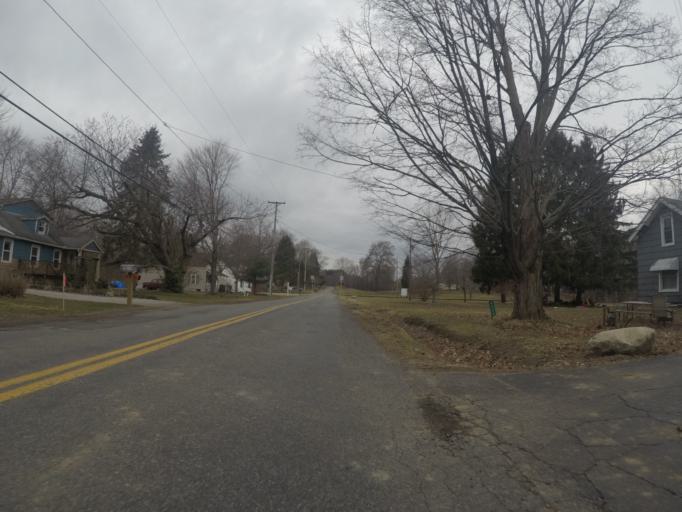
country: US
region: Ohio
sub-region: Portage County
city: Ravenna
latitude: 41.1668
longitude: -81.2826
